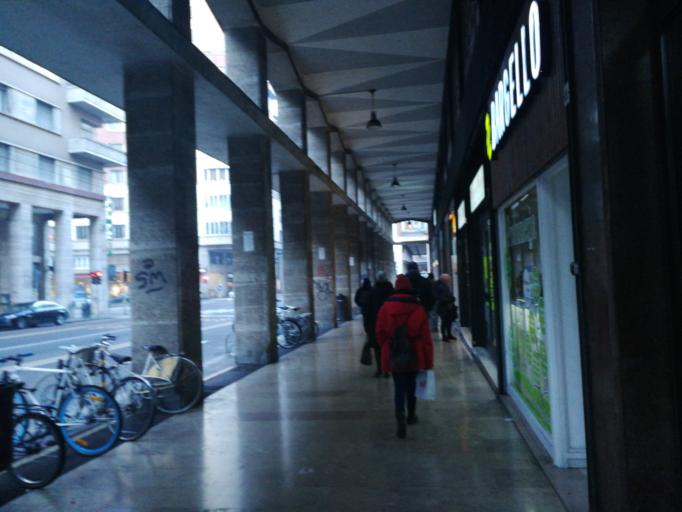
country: IT
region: Emilia-Romagna
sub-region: Provincia di Bologna
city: Bologna
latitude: 44.4982
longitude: 11.3384
